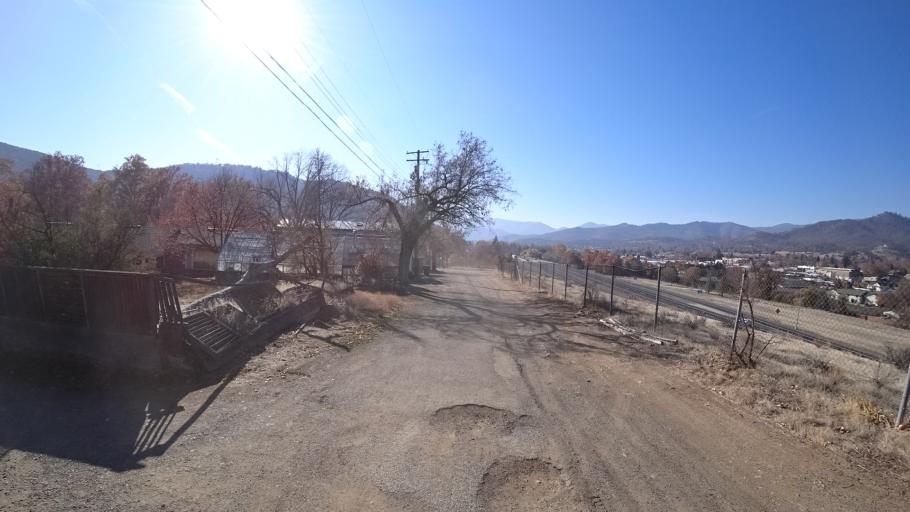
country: US
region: California
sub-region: Siskiyou County
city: Yreka
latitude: 41.7337
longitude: -122.6310
